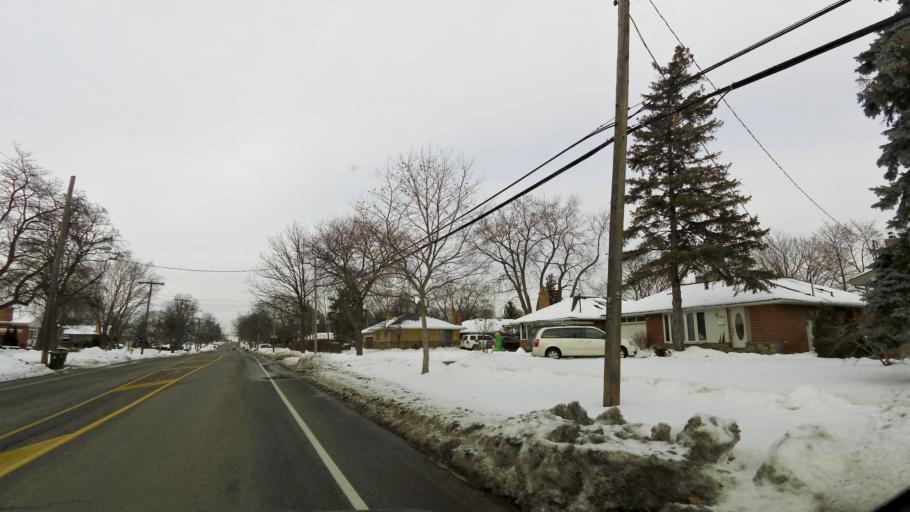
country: CA
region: Ontario
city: Etobicoke
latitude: 43.6654
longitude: -79.5591
